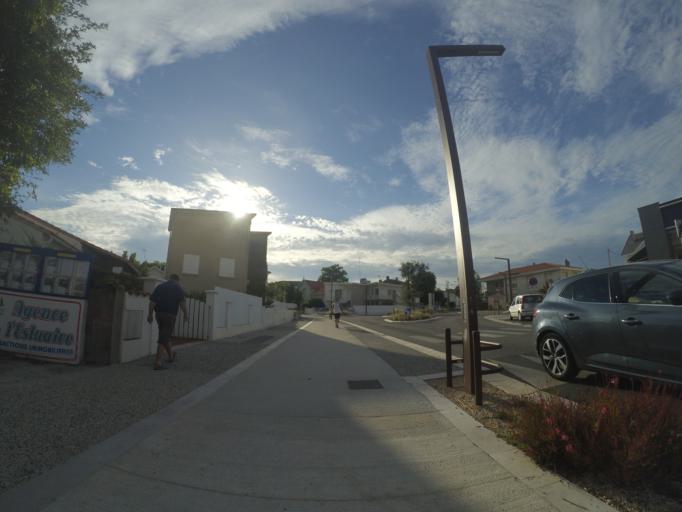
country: FR
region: Poitou-Charentes
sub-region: Departement de la Charente-Maritime
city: Saint-Georges-de-Didonne
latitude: 45.6019
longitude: -1.0018
